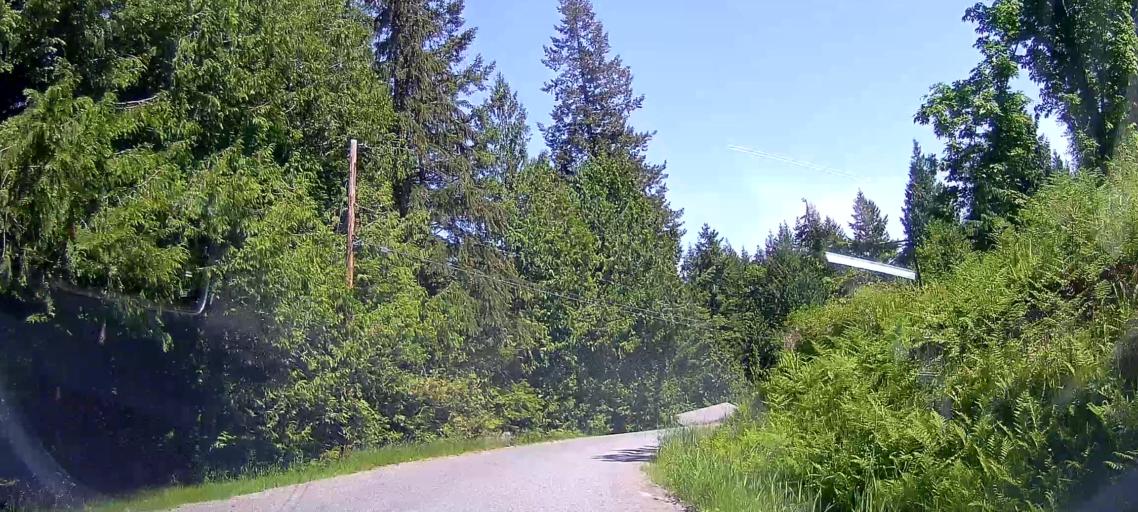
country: US
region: Washington
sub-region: Skagit County
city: Big Lake
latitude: 48.3780
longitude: -122.2652
